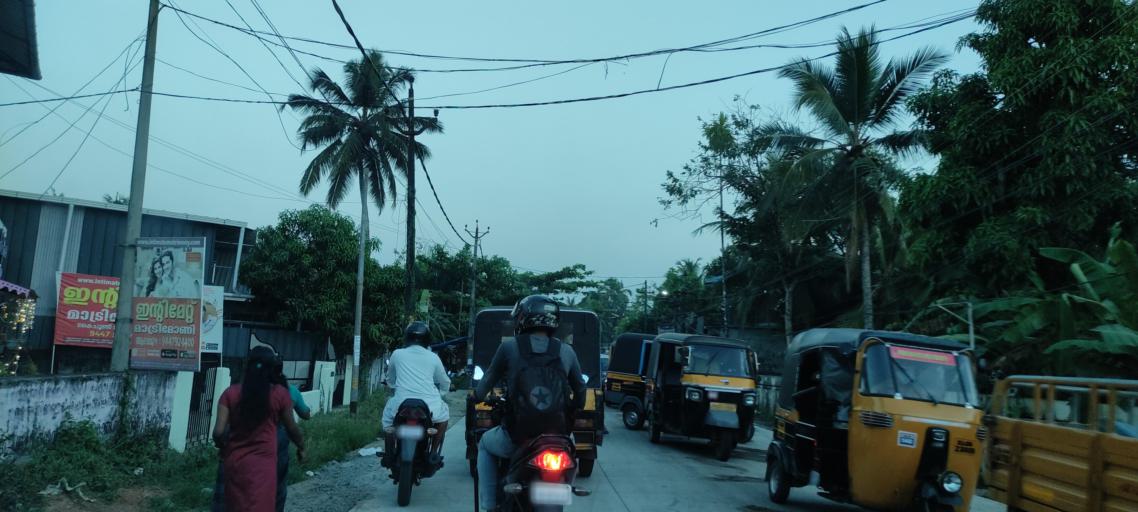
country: IN
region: Kerala
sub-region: Alappuzha
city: Alleppey
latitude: 9.5161
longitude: 76.3353
